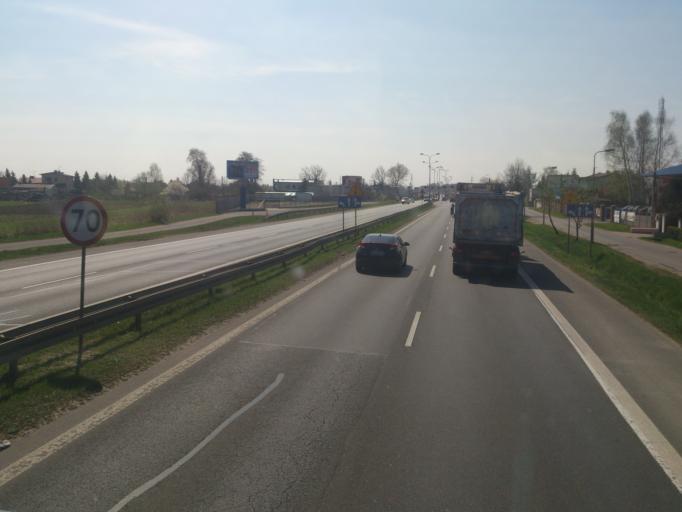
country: PL
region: Lodz Voivodeship
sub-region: Powiat lodzki wschodni
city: Starowa Gora
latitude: 51.6934
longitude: 19.4777
